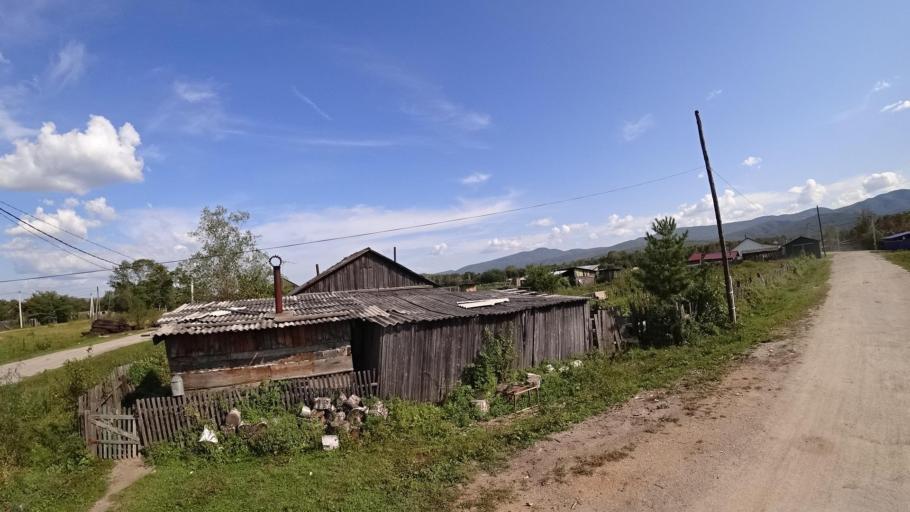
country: RU
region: Jewish Autonomous Oblast
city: Birakan
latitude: 48.9859
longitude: 131.7268
